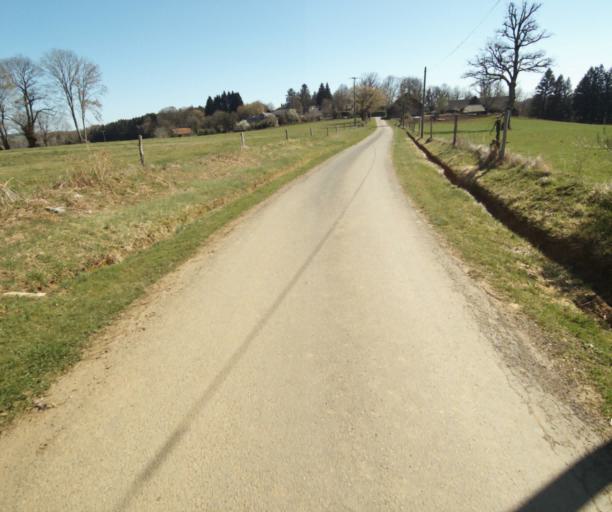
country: FR
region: Limousin
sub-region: Departement de la Correze
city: Seilhac
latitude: 45.3839
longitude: 1.6856
